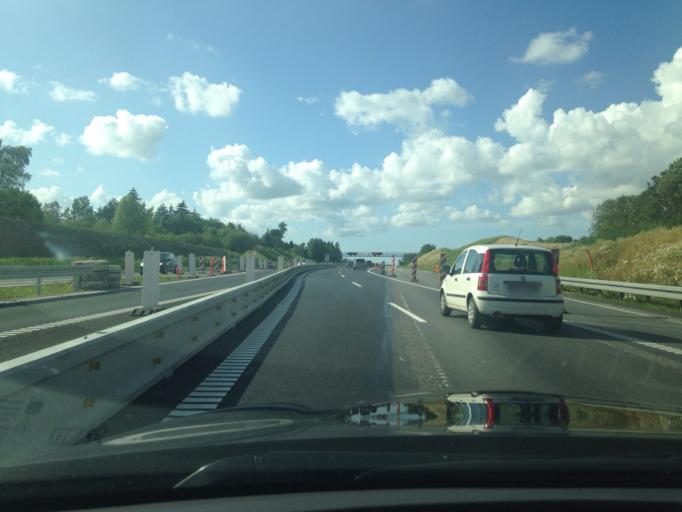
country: DK
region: Capital Region
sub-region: Horsholm Kommune
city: Horsholm
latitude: 55.8477
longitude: 12.5055
